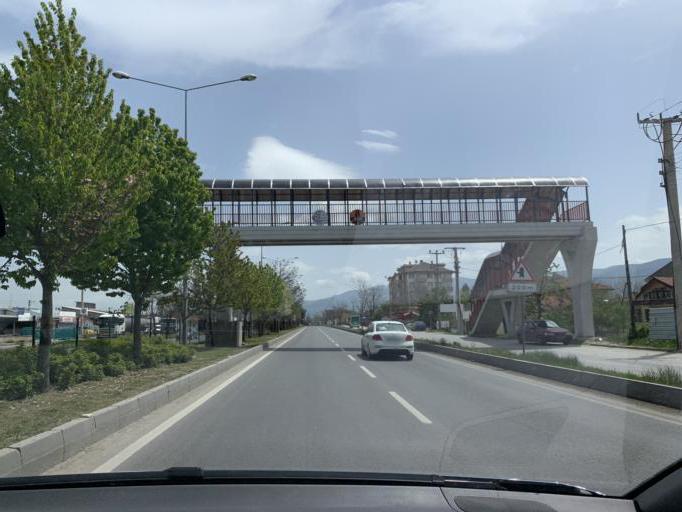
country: TR
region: Bolu
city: Bolu
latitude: 40.7367
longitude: 31.6223
